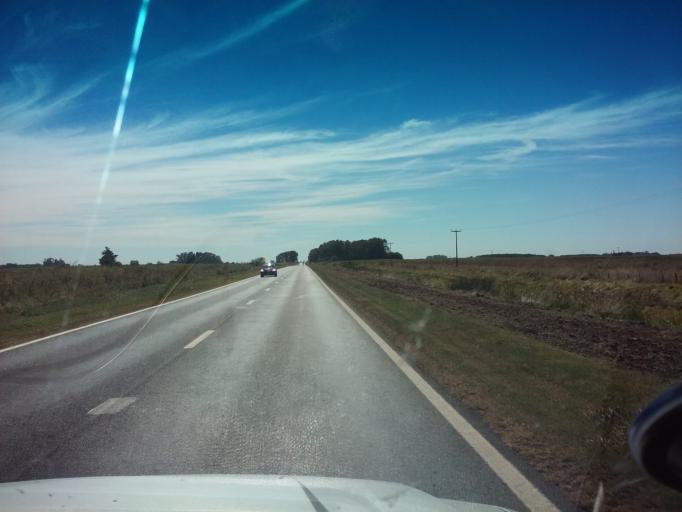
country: AR
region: Buenos Aires
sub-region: Partido de Nueve de Julio
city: Nueve de Julio
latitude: -35.3498
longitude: -60.6881
